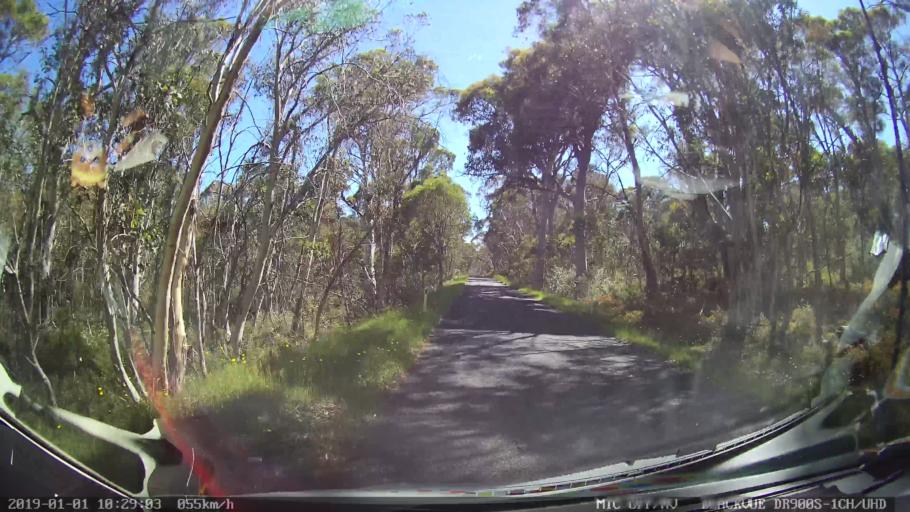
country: AU
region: New South Wales
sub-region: Snowy River
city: Jindabyne
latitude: -36.0567
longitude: 148.2450
